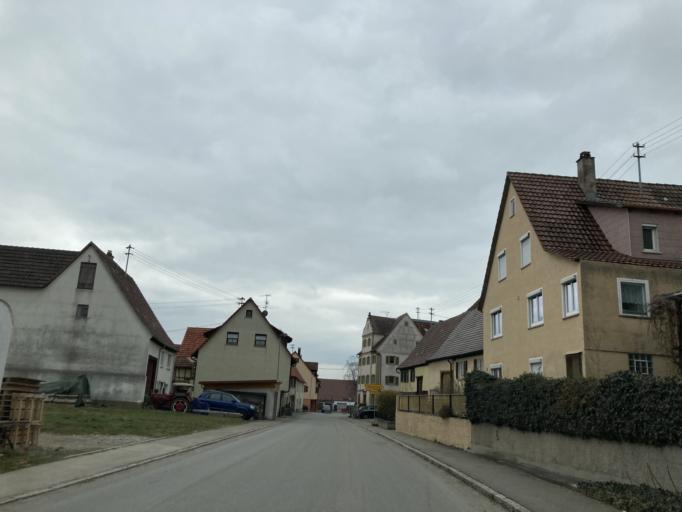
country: DE
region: Baden-Wuerttemberg
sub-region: Tuebingen Region
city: Hirrlingen
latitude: 48.4246
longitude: 8.8466
